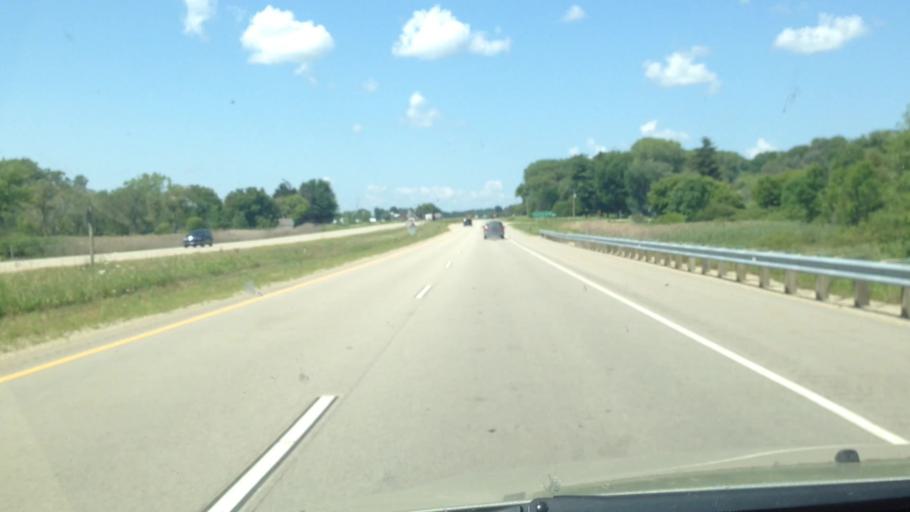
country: US
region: Wisconsin
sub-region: Oconto County
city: Oconto Falls
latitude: 44.8007
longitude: -88.0031
